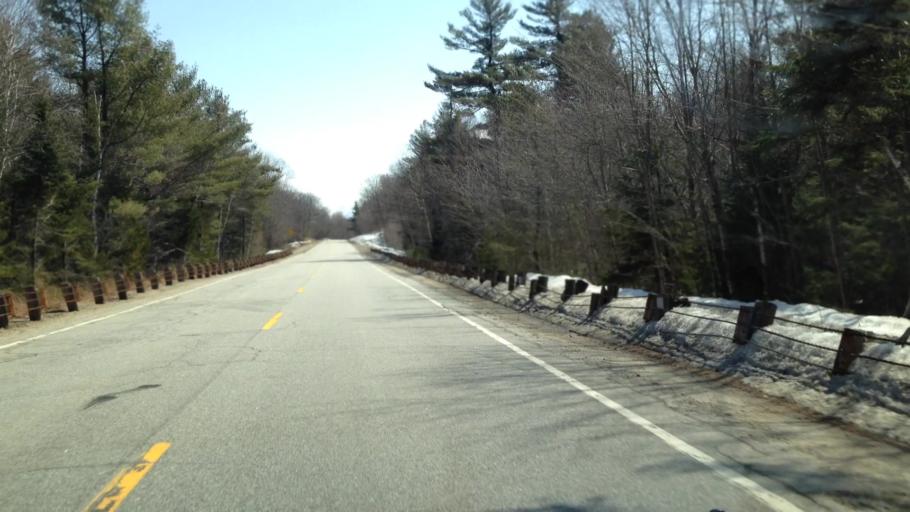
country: US
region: New Hampshire
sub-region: Sullivan County
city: Springfield
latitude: 43.4918
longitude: -71.9868
